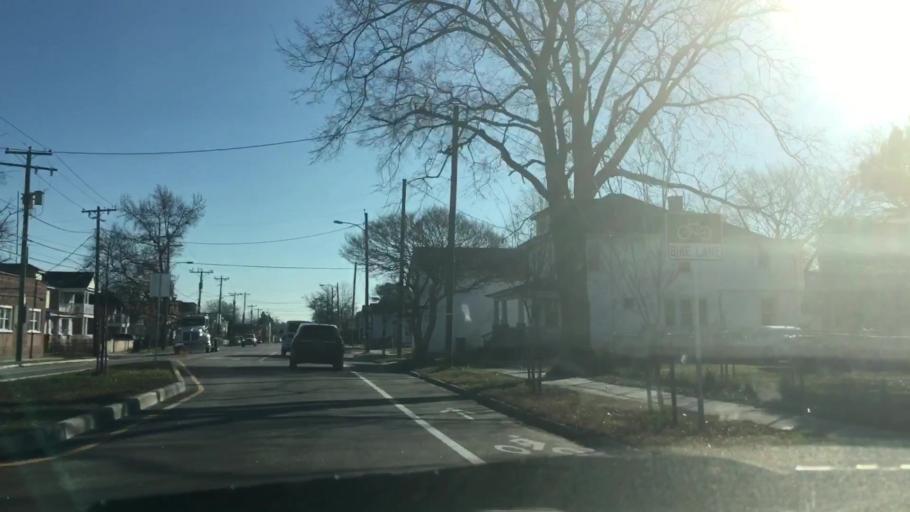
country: US
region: Virginia
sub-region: City of Norfolk
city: Norfolk
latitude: 36.8772
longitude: -76.2618
